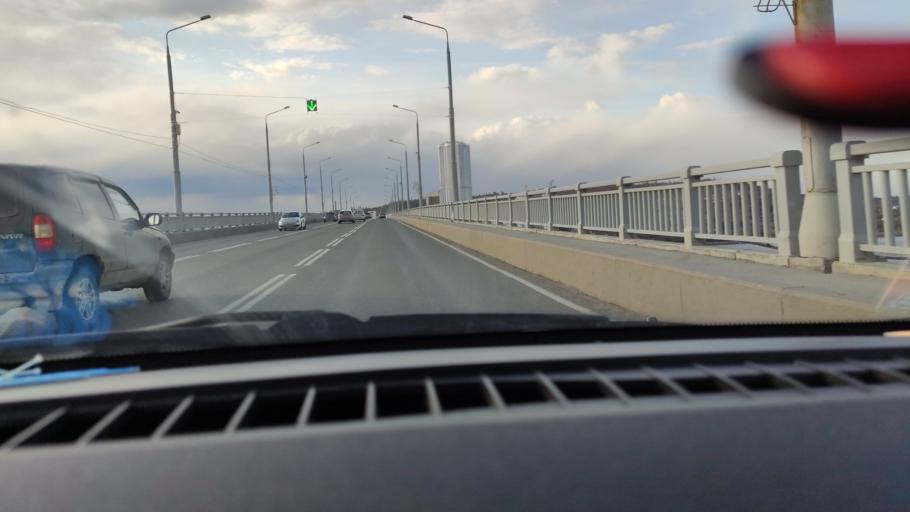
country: RU
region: Saratov
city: Engel's
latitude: 51.5243
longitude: 46.0662
